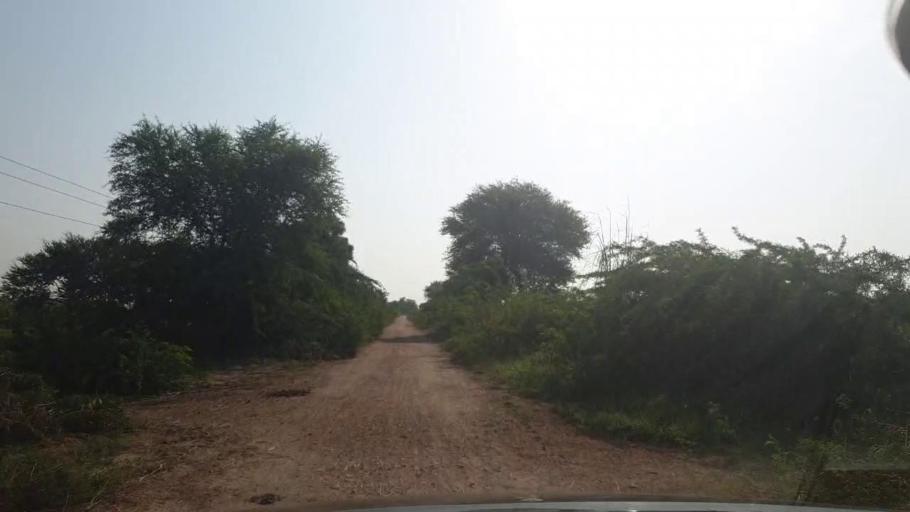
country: PK
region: Sindh
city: Tando Bago
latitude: 24.6509
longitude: 69.1706
